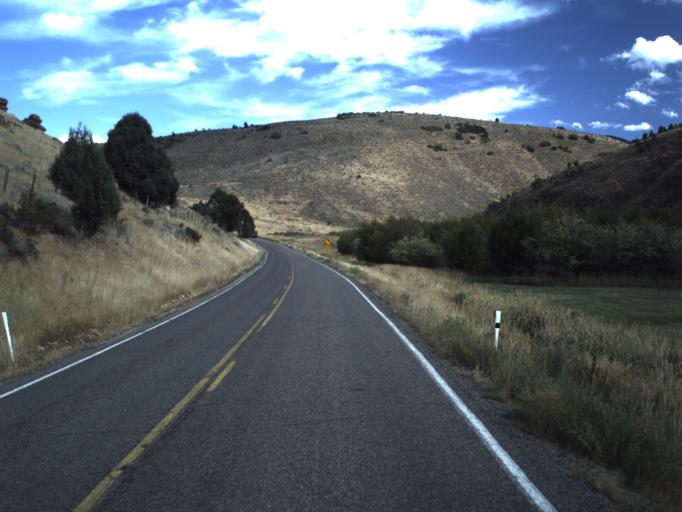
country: US
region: Utah
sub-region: Cache County
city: Millville
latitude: 41.6033
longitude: -111.5760
